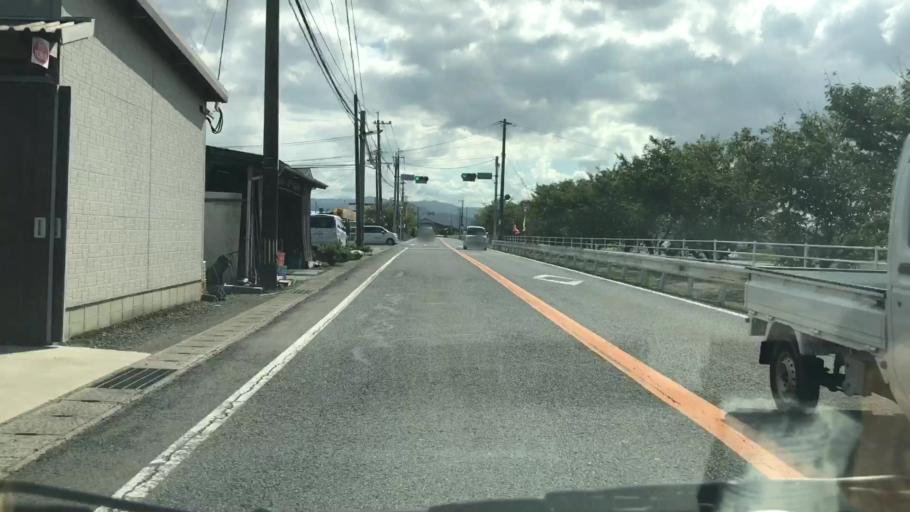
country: JP
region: Saga Prefecture
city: Kashima
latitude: 33.1603
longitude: 130.1643
